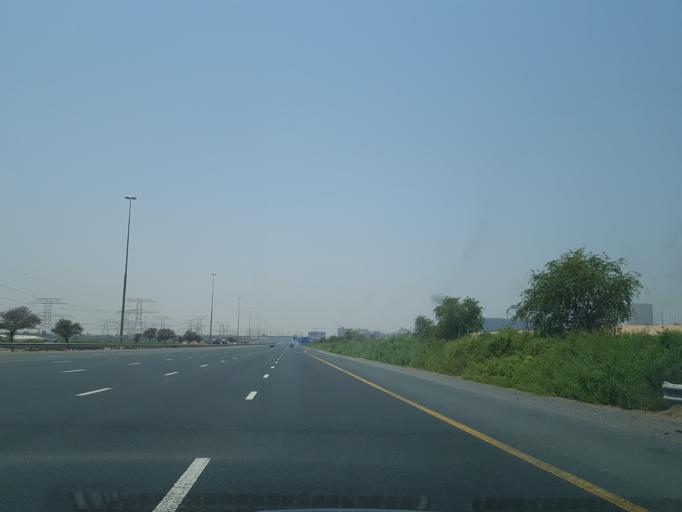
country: AE
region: Dubai
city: Dubai
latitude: 25.0962
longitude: 55.4046
